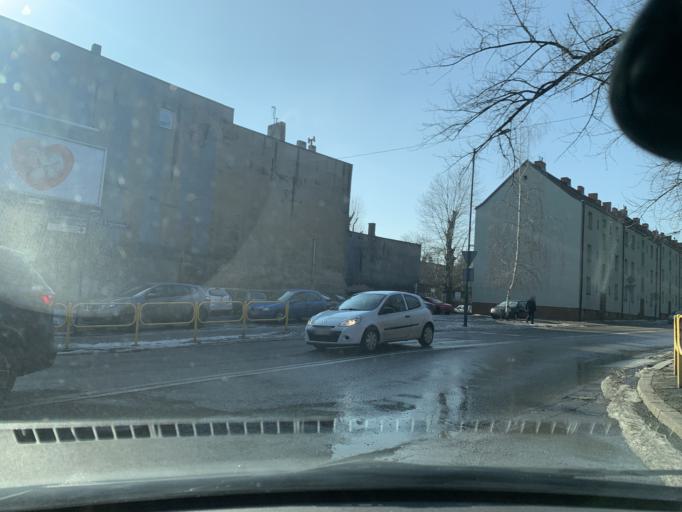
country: PL
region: Silesian Voivodeship
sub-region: Bytom
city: Bytom
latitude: 50.3528
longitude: 18.9200
